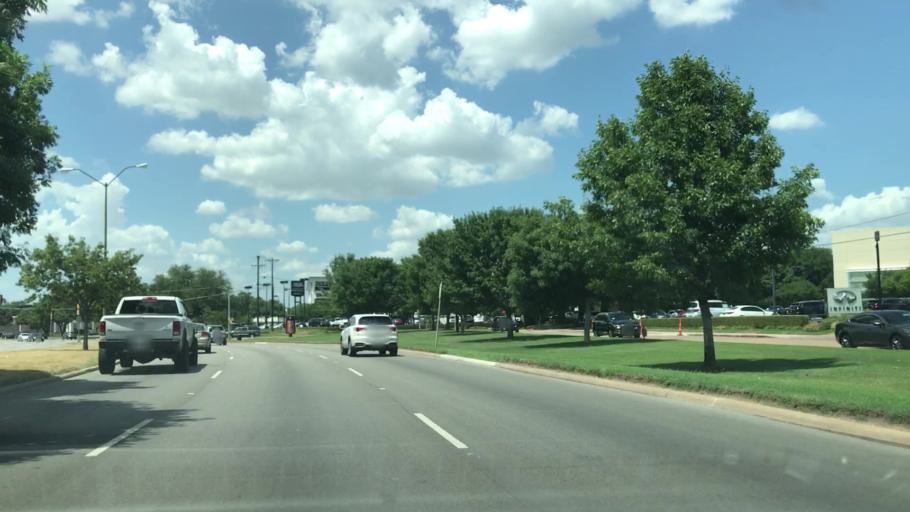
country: US
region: Texas
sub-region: Dallas County
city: University Park
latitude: 32.8437
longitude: -96.8345
